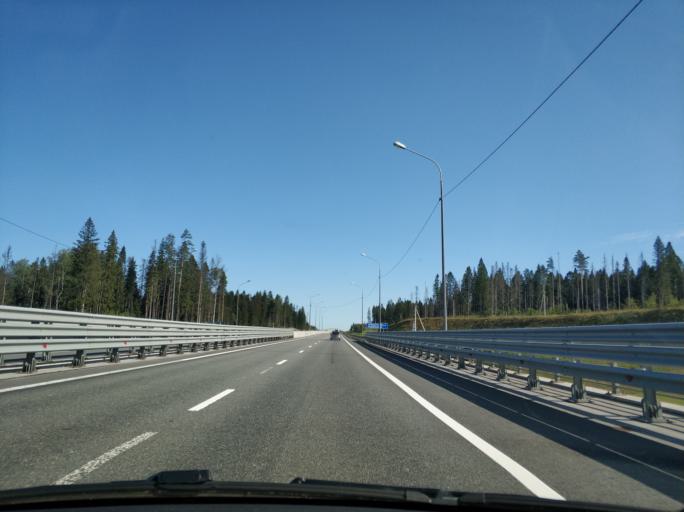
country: RU
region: Leningrad
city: Sosnovo
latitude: 60.4599
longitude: 30.1963
